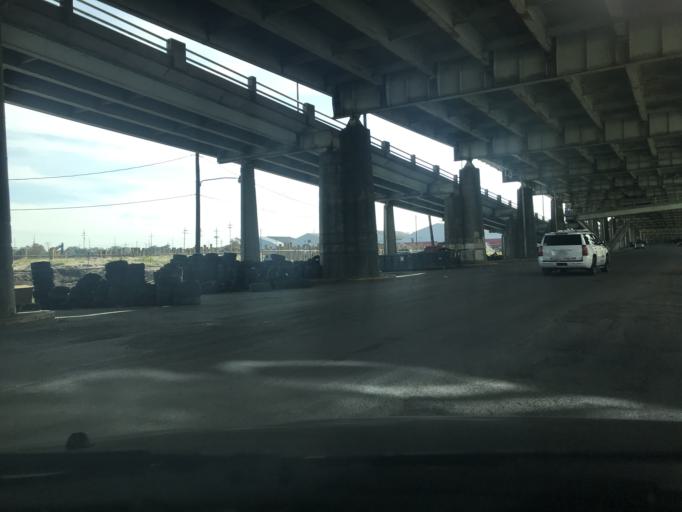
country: US
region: Louisiana
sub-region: Orleans Parish
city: New Orleans
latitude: 29.9573
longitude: -90.0946
